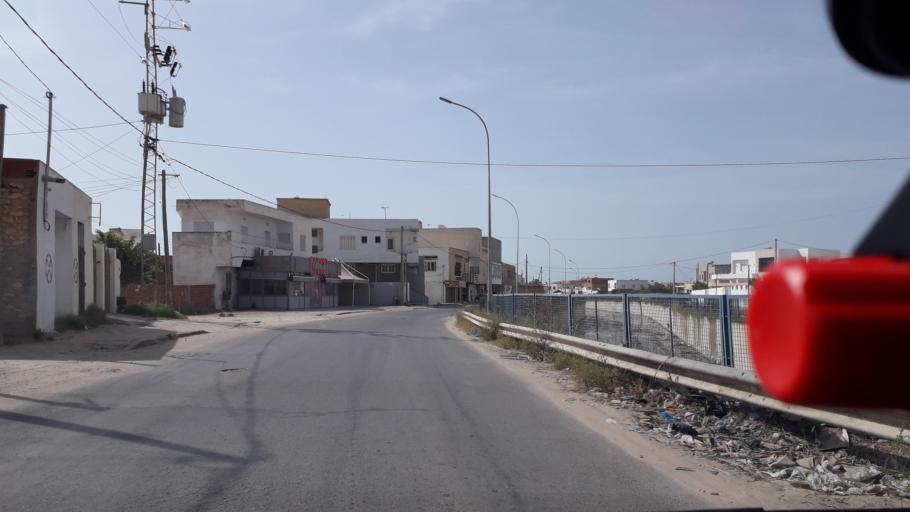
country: TN
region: Safaqis
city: Al Qarmadah
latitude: 34.7976
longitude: 10.7722
